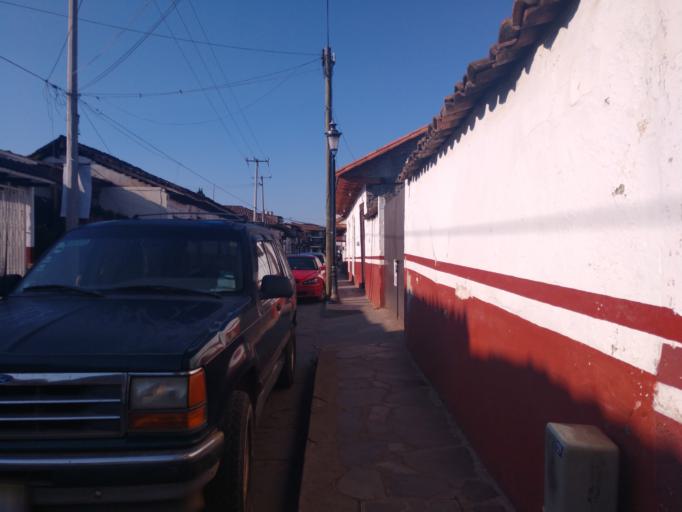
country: MX
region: Jalisco
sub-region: Mazamitla
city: Mazamitla
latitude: 19.9174
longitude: -103.0193
